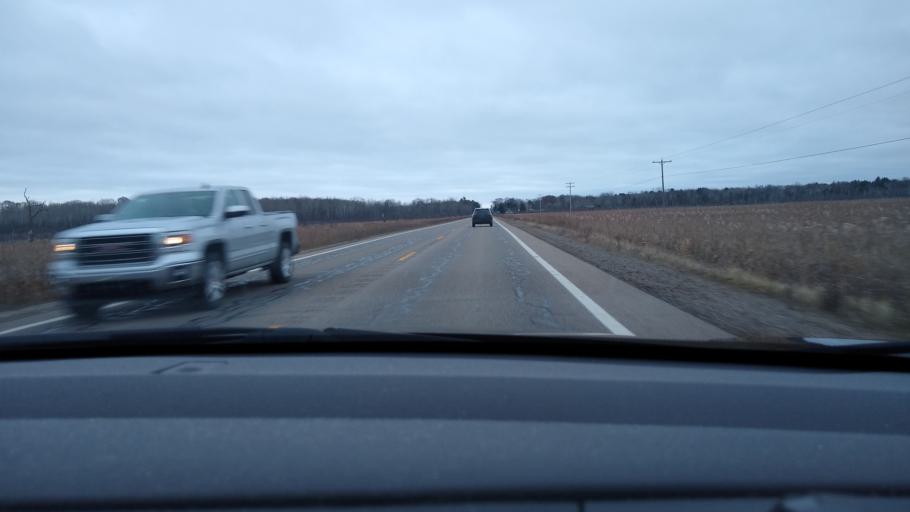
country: US
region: Michigan
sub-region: Roscommon County
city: Houghton Lake
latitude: 44.3358
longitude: -84.8276
